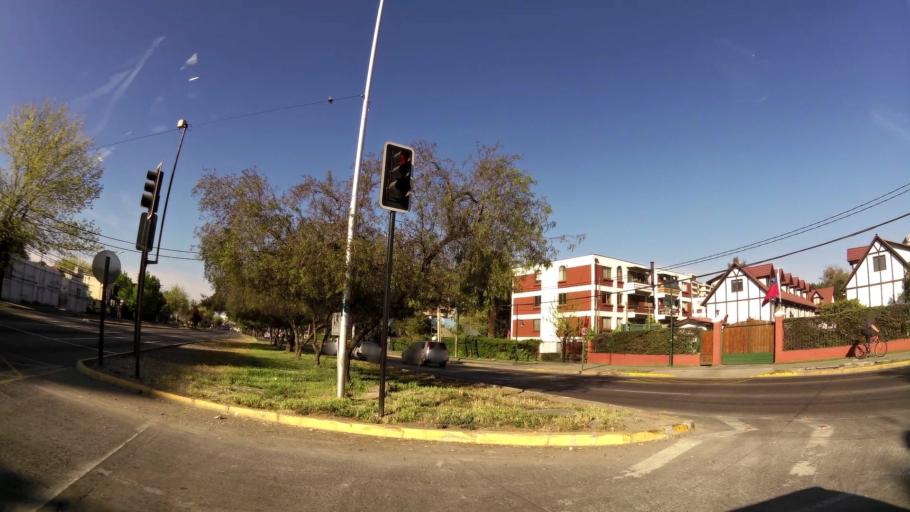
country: CL
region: Santiago Metropolitan
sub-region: Provincia de Santiago
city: Villa Presidente Frei, Nunoa, Santiago, Chile
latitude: -33.4555
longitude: -70.5714
